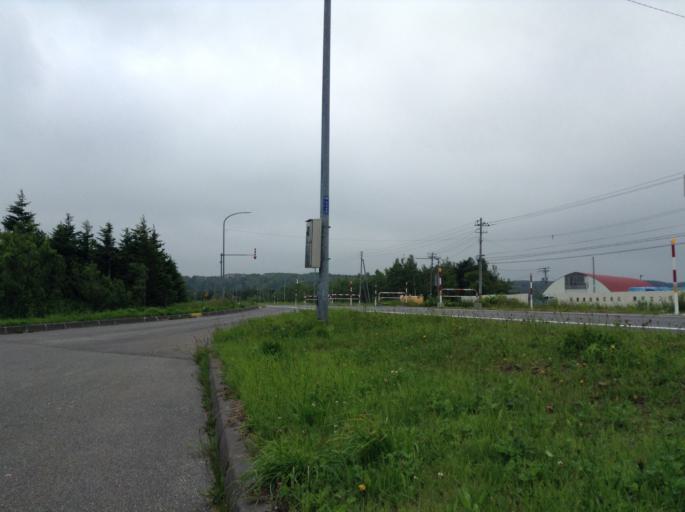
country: JP
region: Hokkaido
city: Wakkanai
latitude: 45.3635
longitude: 141.7296
